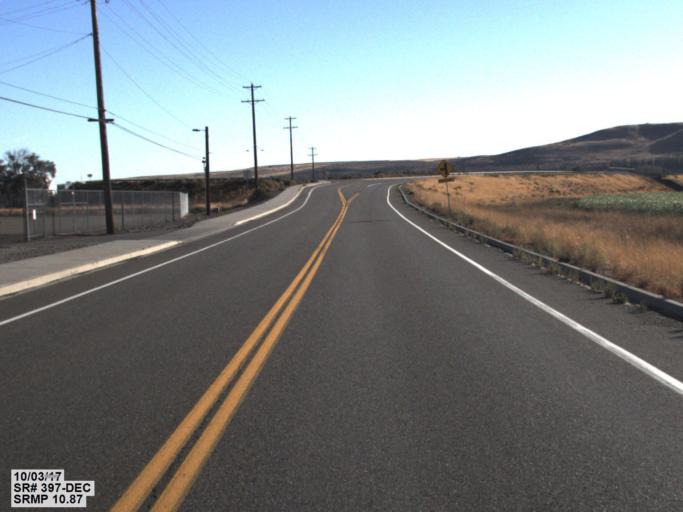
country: US
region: Washington
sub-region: Benton County
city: Finley
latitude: 46.1451
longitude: -119.0128
